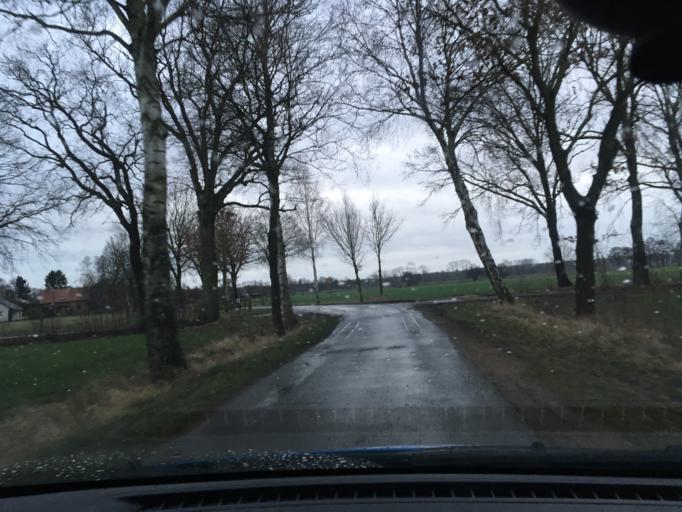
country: DE
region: Lower Saxony
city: Ludersburg
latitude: 53.3113
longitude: 10.6052
